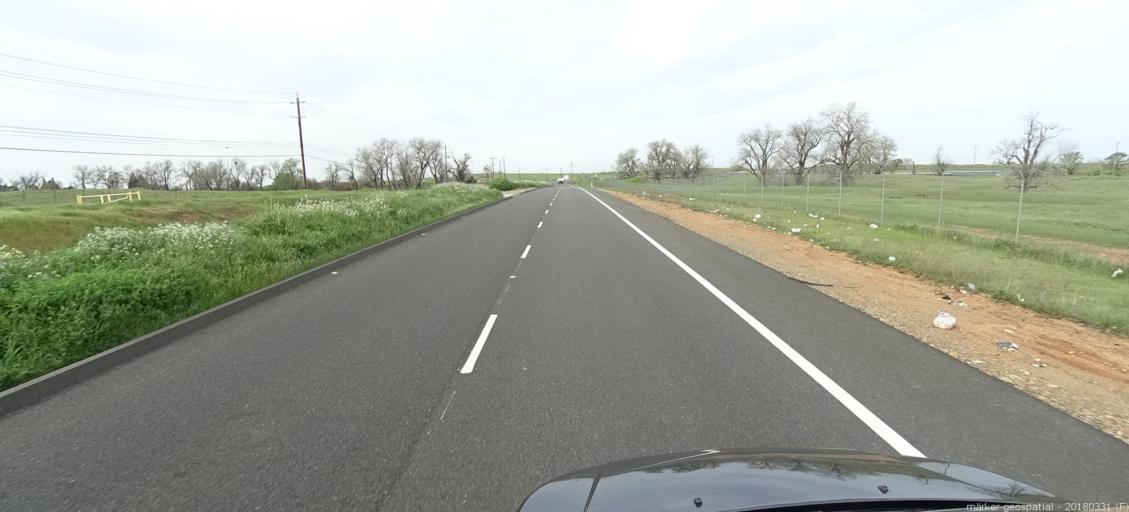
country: US
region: California
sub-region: Sacramento County
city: Folsom
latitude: 38.6105
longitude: -121.1628
